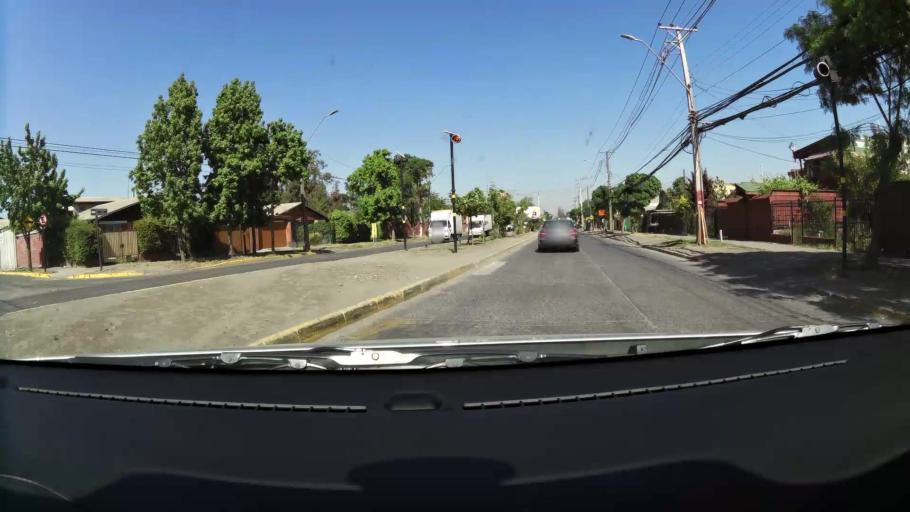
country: CL
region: Santiago Metropolitan
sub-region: Provincia de Maipo
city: San Bernardo
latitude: -33.5595
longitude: -70.7067
